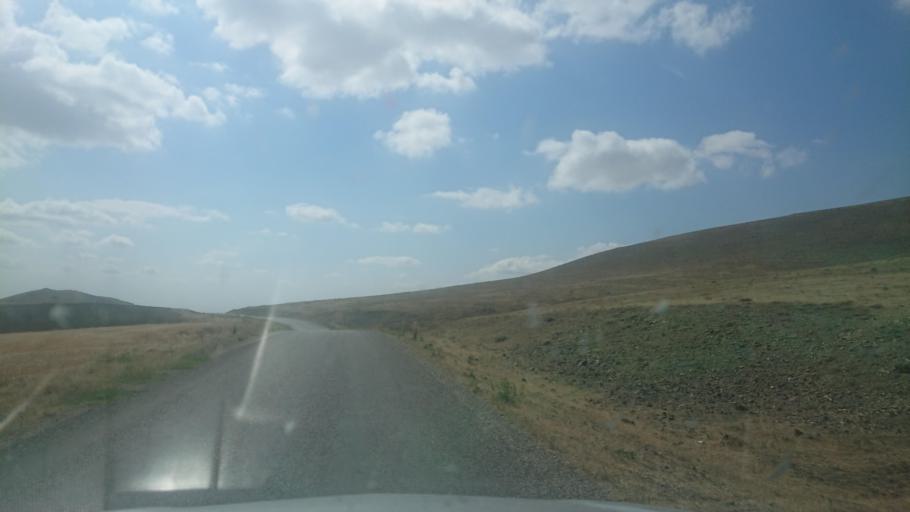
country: TR
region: Aksaray
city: Sariyahsi
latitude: 39.0026
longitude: 33.9700
